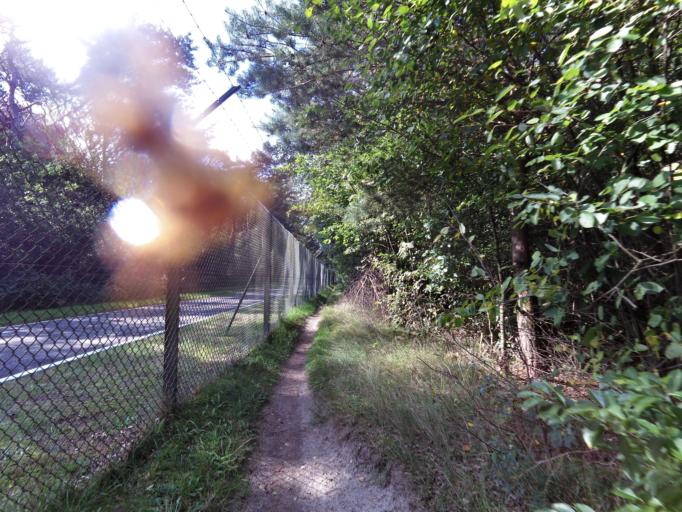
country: NL
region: North Brabant
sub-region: Gemeente Woensdrecht
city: Woensdrecht
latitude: 51.4574
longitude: 4.3541
